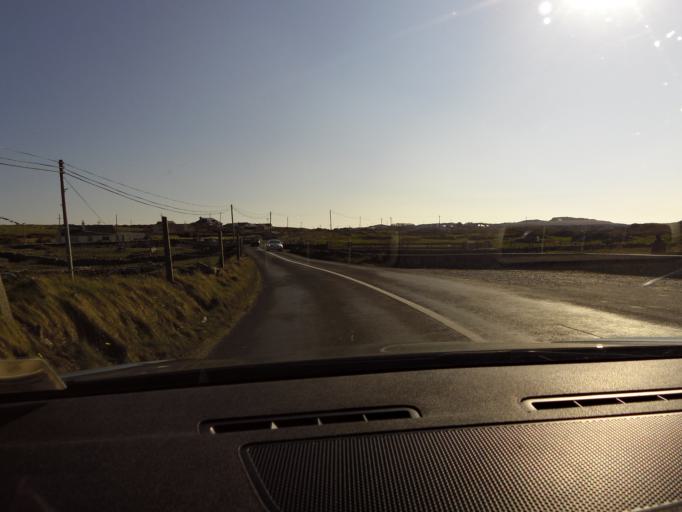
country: IE
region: Connaught
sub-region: County Galway
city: Clifden
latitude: 53.4418
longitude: -10.0640
